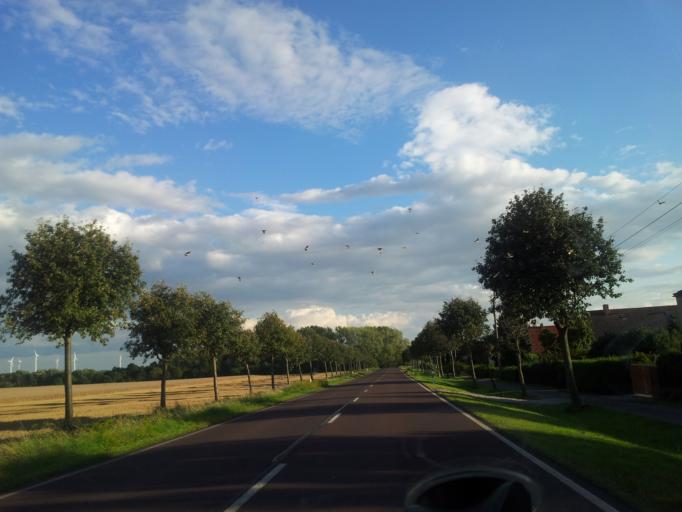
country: DE
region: Saxony-Anhalt
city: Gross Bornecke
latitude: 51.8226
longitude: 11.4569
